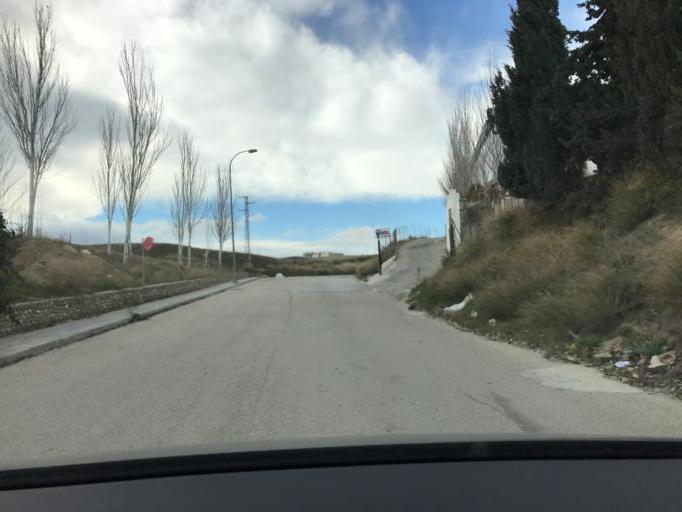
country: ES
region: Andalusia
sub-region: Provincia de Granada
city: Alhendin
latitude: 37.0983
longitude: -3.6560
